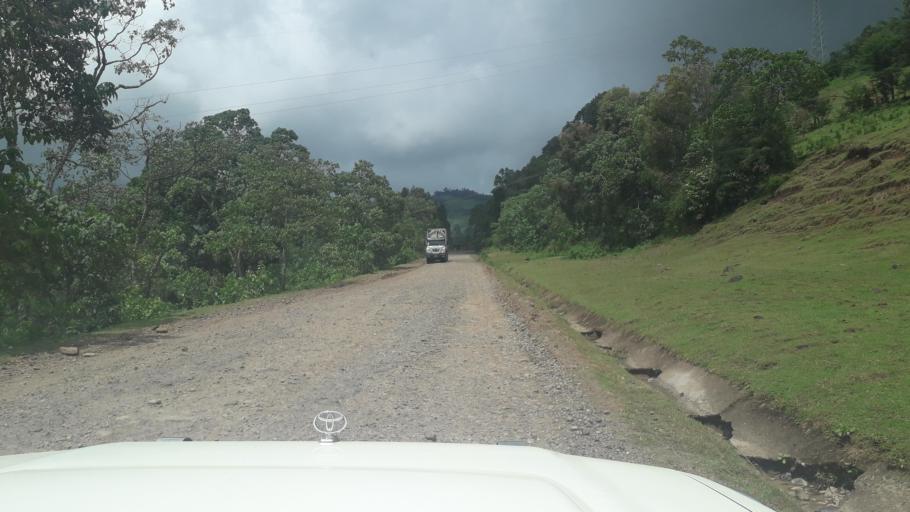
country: ET
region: Oromiya
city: Jima
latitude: 7.4309
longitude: 36.8760
